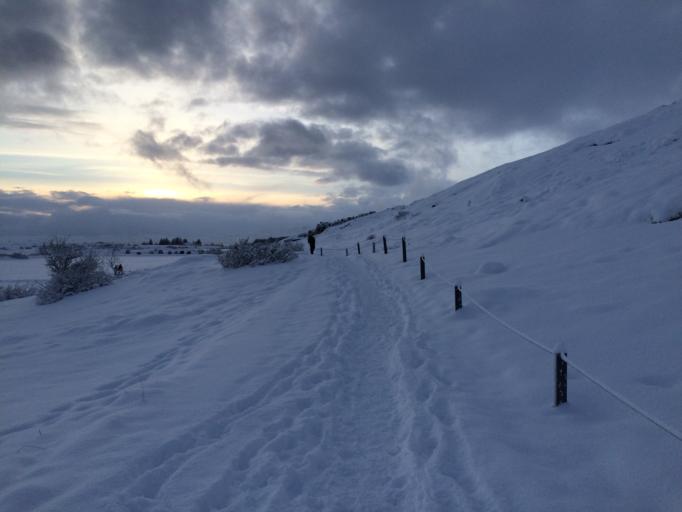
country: IS
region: South
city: Hveragerdi
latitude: 64.2660
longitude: -21.1155
